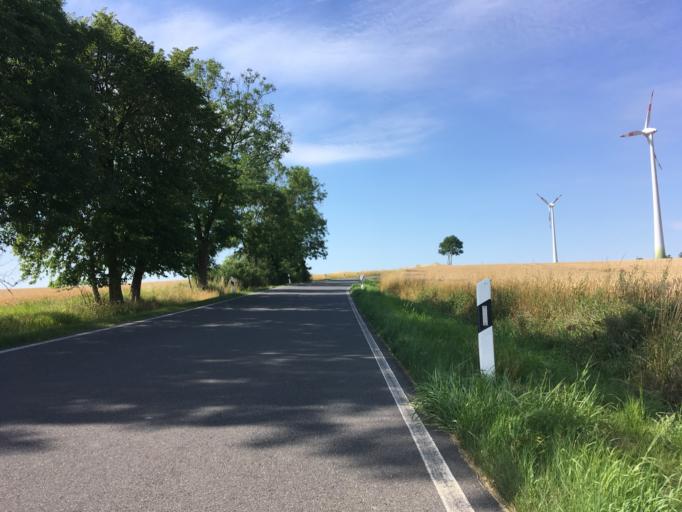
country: DE
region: Brandenburg
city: Gramzow
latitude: 53.2580
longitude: 14.0629
